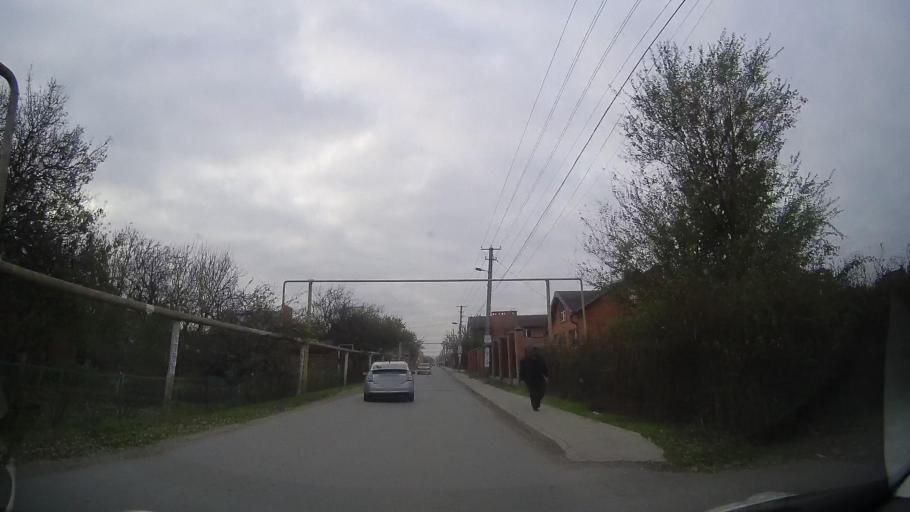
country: RU
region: Rostov
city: Bataysk
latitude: 47.0862
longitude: 39.7608
